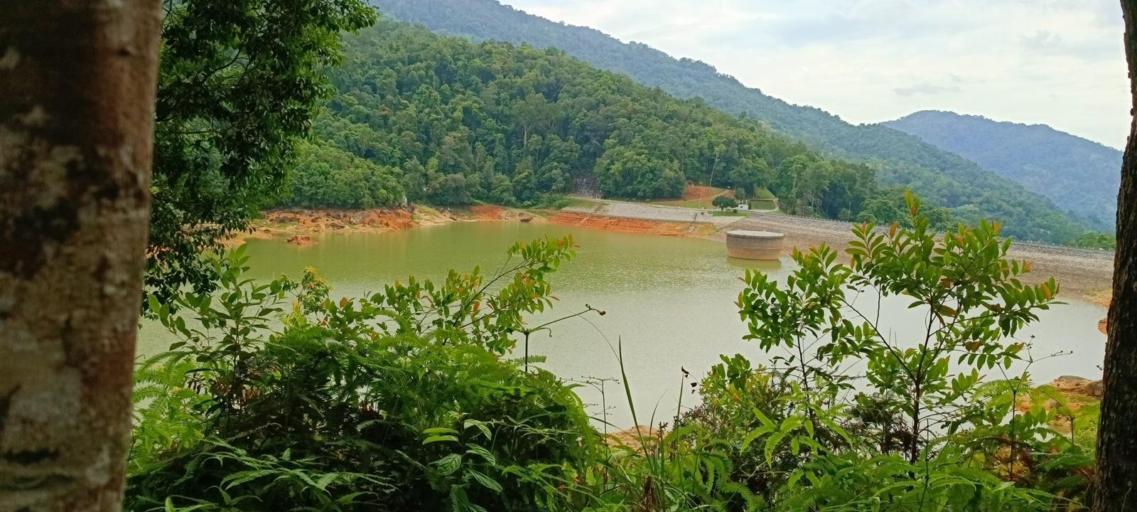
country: MY
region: Penang
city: Kampung Sungai Ara
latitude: 5.3932
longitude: 100.2615
